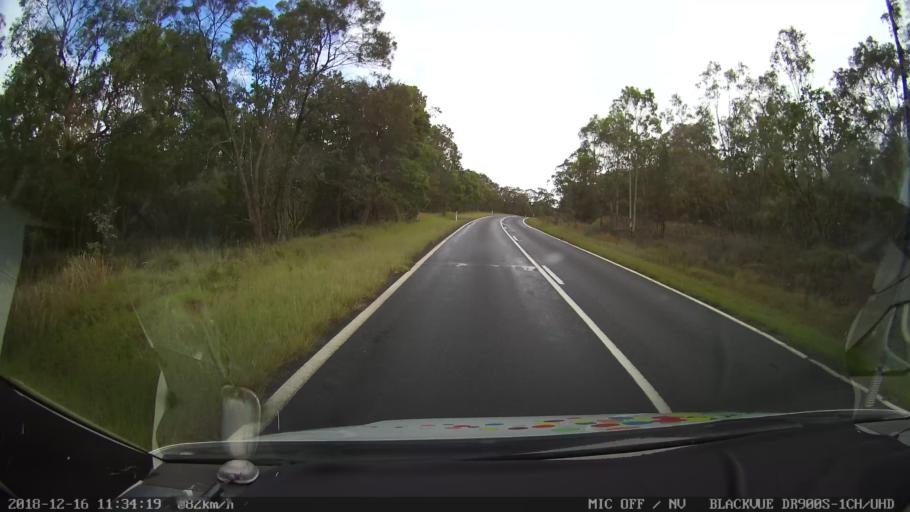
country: AU
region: New South Wales
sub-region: Tenterfield Municipality
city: Carrolls Creek
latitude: -29.0000
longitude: 152.1530
